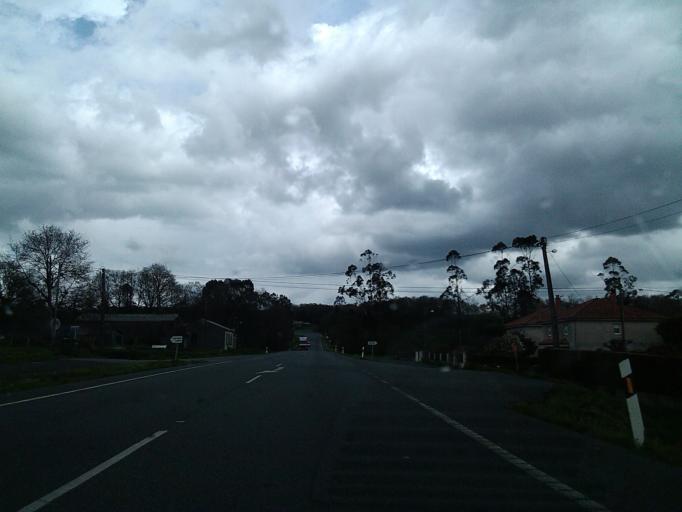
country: ES
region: Galicia
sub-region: Provincia da Coruna
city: Vilasantar
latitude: 43.1166
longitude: -8.1052
